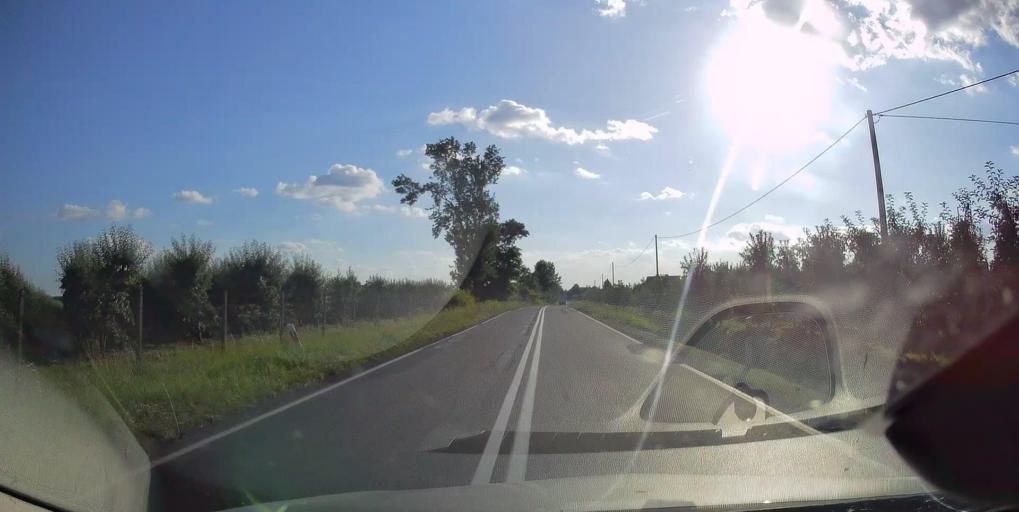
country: PL
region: Masovian Voivodeship
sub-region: Powiat grojecki
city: Bledow
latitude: 51.8015
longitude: 20.6310
